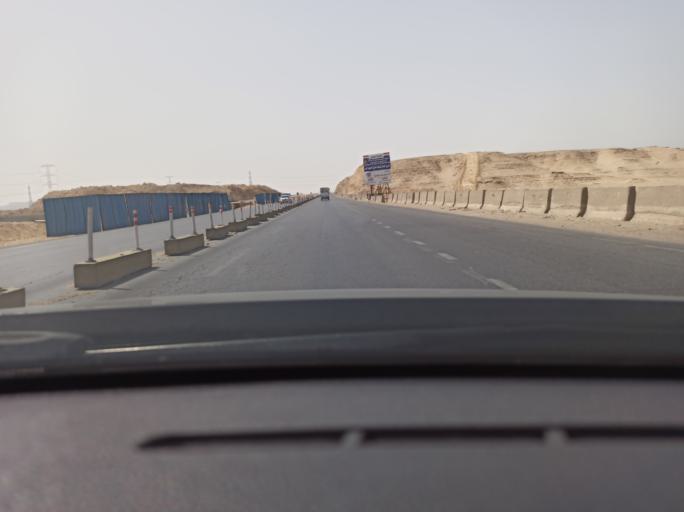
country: EG
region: Muhafazat Bani Suwayf
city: Bush
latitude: 29.1544
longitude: 31.2346
